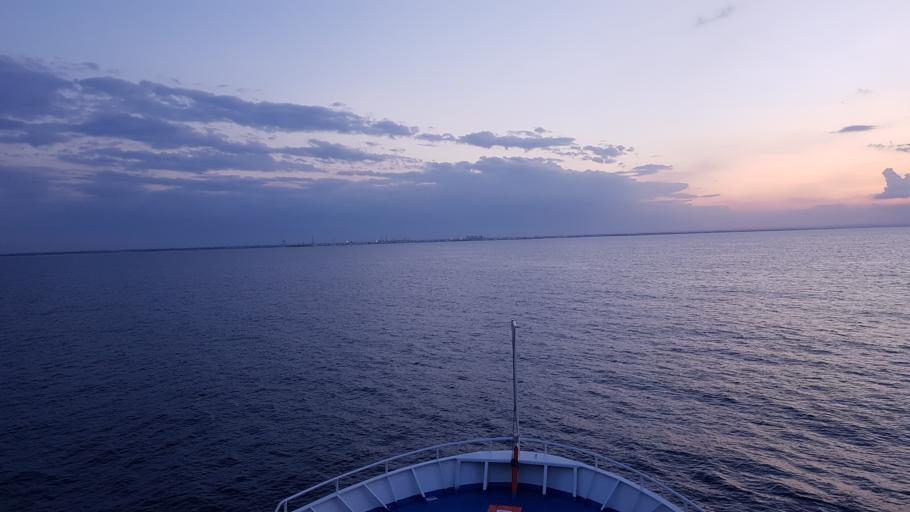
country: IT
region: Apulia
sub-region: Provincia di Brindisi
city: Materdomini
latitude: 40.6721
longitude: 18.0824
